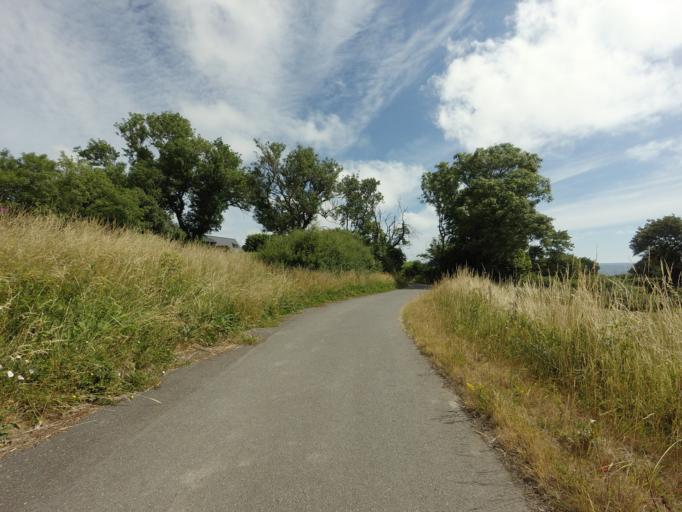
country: SE
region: Skane
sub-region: Simrishamns Kommun
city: Simrishamn
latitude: 55.5043
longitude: 14.3292
